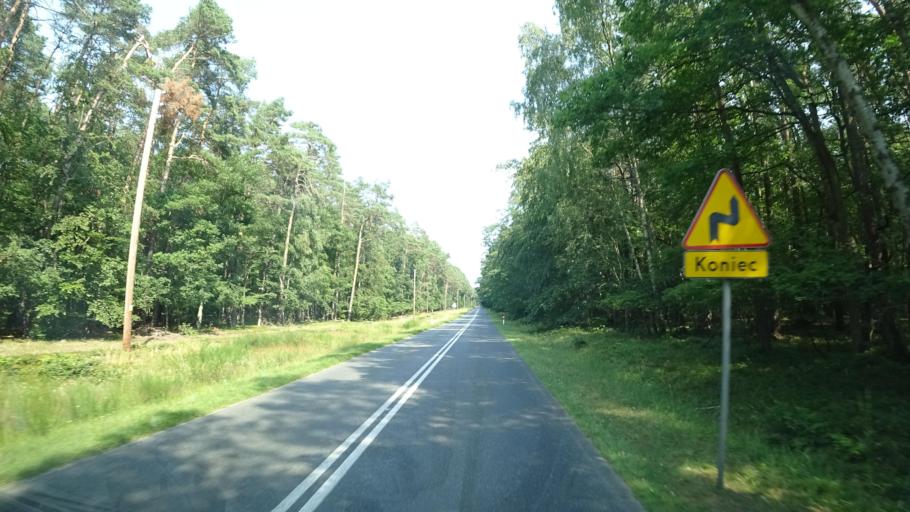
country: PL
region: West Pomeranian Voivodeship
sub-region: Powiat kamienski
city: Miedzyzdroje
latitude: 53.9640
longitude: 14.5446
